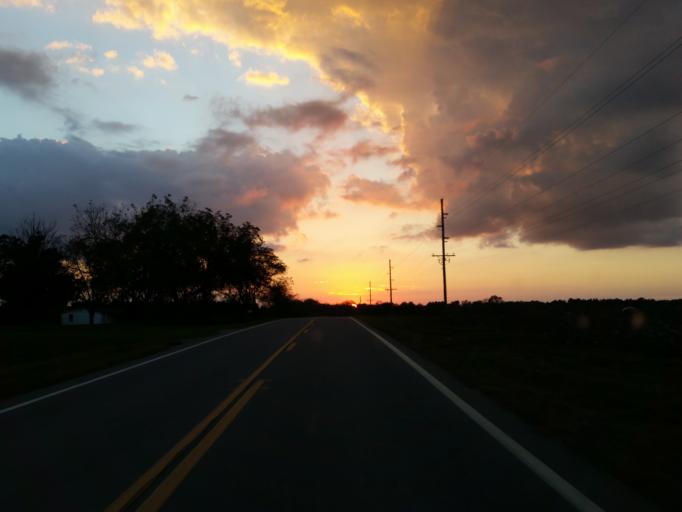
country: US
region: Georgia
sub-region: Dooly County
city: Unadilla
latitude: 32.1457
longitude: -83.6673
